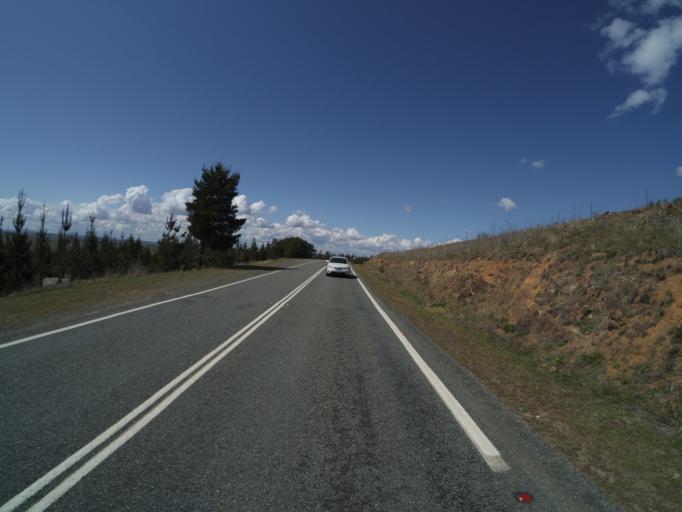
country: AU
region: Australian Capital Territory
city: Macquarie
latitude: -35.3033
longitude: 148.9441
